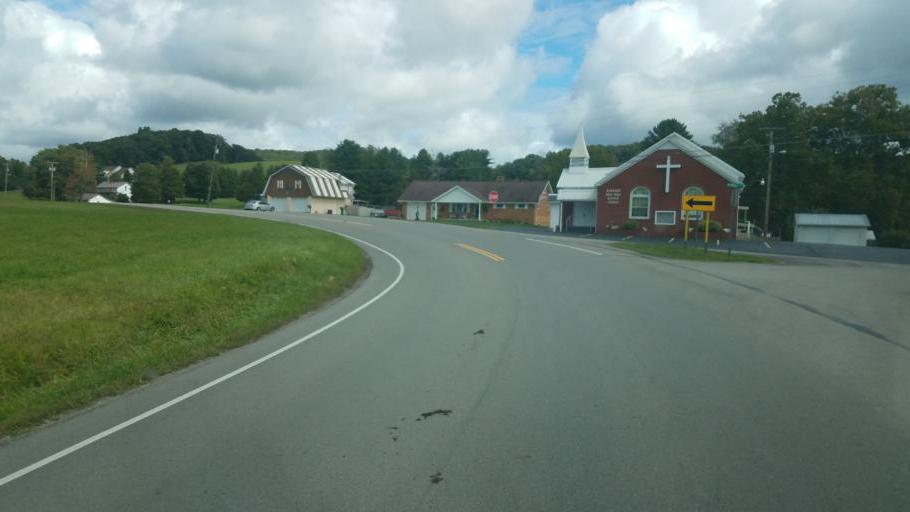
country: US
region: Ohio
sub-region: Scioto County
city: Sciotodale
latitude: 38.8659
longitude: -82.8390
